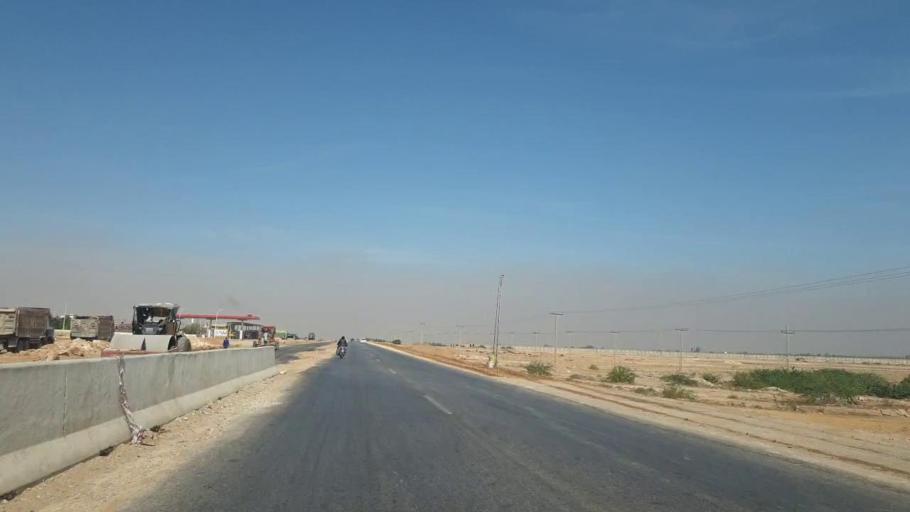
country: PK
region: Sindh
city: Jamshoro
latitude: 25.4979
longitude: 68.2725
